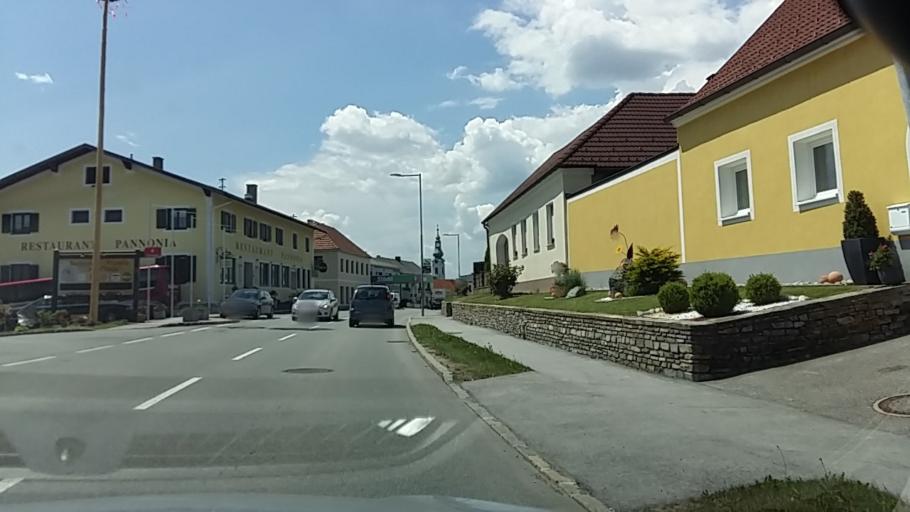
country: AT
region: Burgenland
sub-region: Politischer Bezirk Oberwart
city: Bernstein
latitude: 47.4071
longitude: 16.2621
